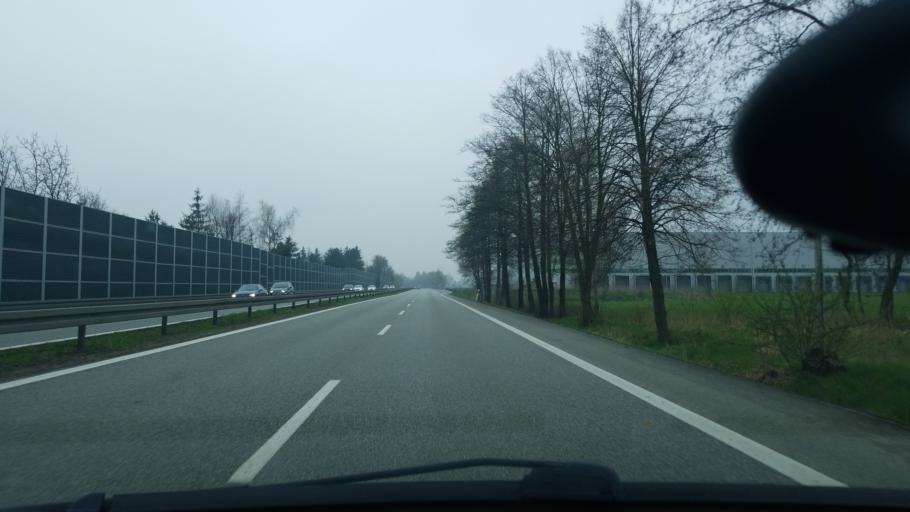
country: PL
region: Silesian Voivodeship
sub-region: Powiat pszczynski
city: Pawlowice
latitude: 49.9885
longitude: 18.7125
